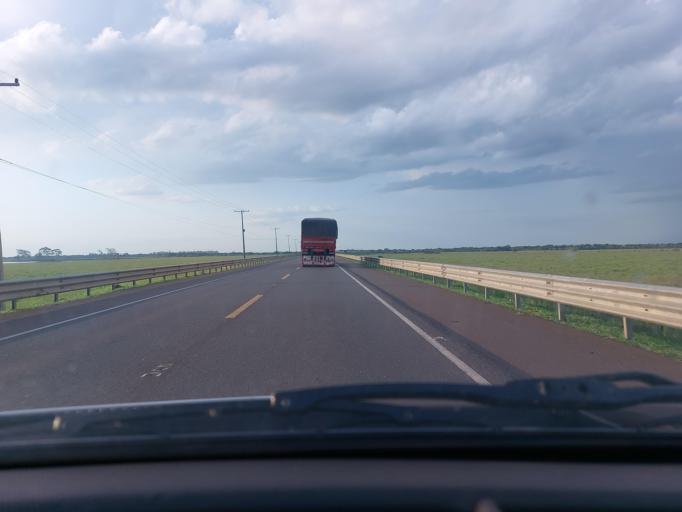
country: PY
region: Cordillera
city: Arroyos y Esteros
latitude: -25.0245
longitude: -57.0339
